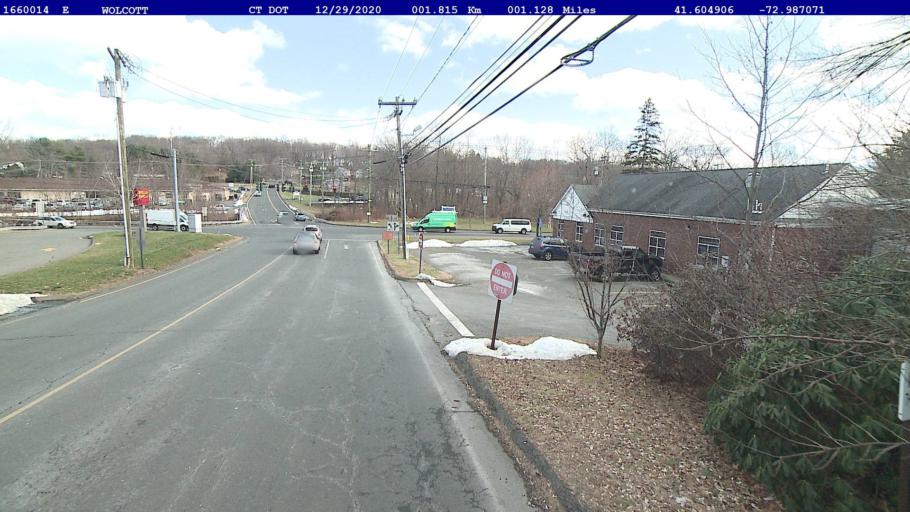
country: US
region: Connecticut
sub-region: New Haven County
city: Wolcott
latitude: 41.6049
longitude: -72.9871
